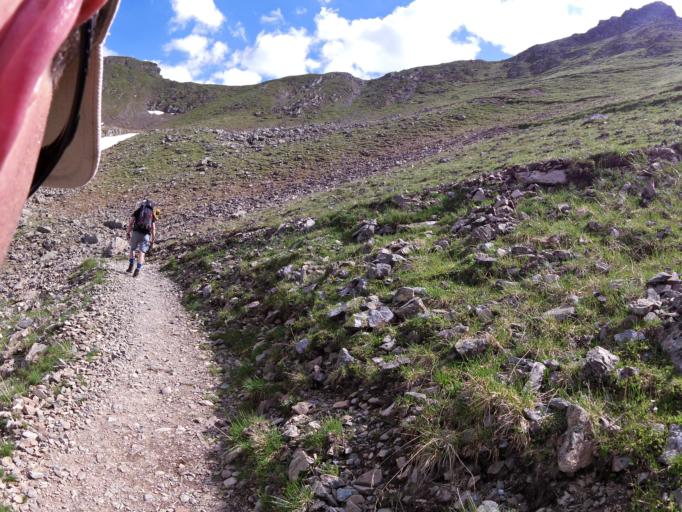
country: AT
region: Tyrol
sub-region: Politischer Bezirk Innsbruck Land
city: Gschnitz
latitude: 47.0458
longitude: 11.3111
